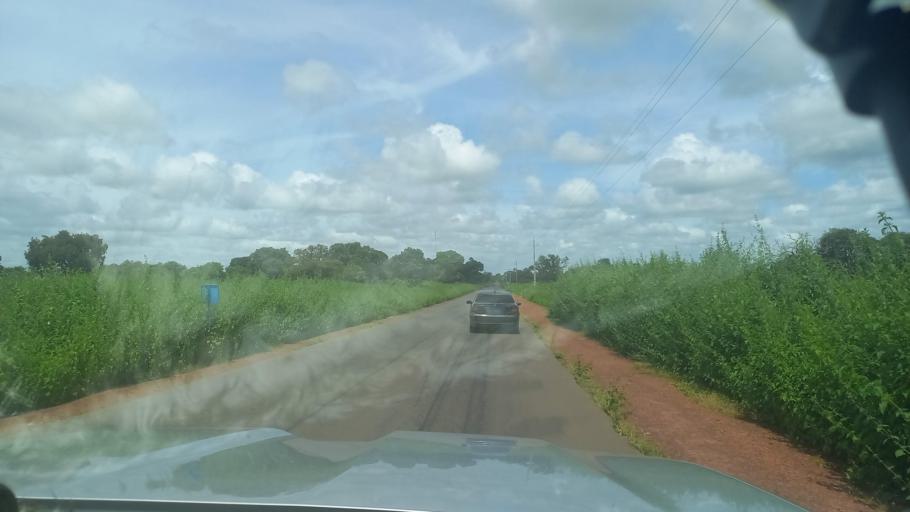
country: GM
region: Lower River
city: Kaiaf
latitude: 13.2003
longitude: -15.5514
